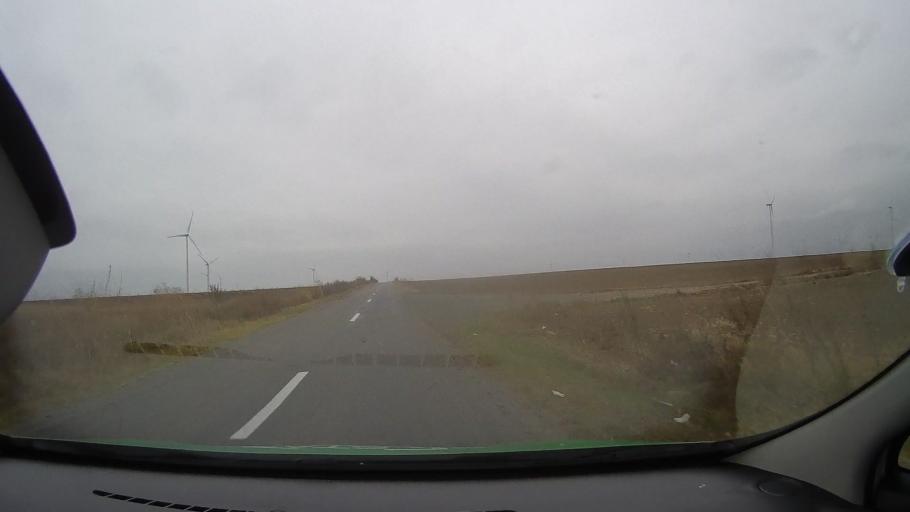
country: RO
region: Constanta
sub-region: Comuna Pantelimon
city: Pantelimon
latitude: 44.5074
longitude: 28.3439
